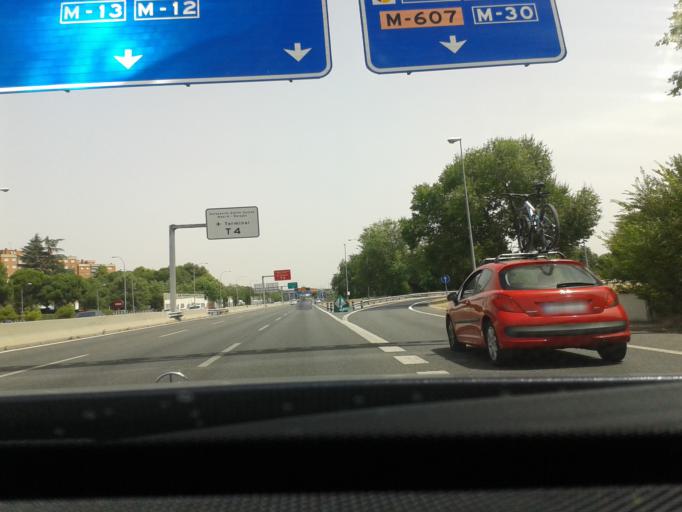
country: ES
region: Madrid
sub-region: Provincia de Madrid
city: Barajas de Madrid
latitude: 40.4571
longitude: -3.5819
